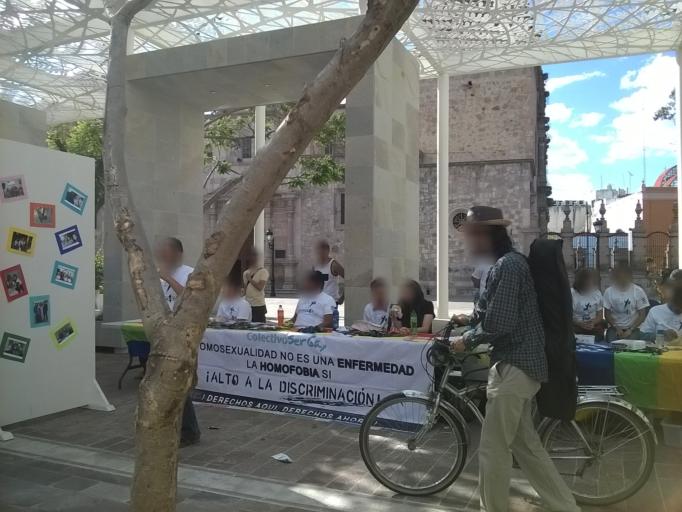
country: MX
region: Aguascalientes
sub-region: Aguascalientes
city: Aguascalientes
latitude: 21.8803
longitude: -102.2967
